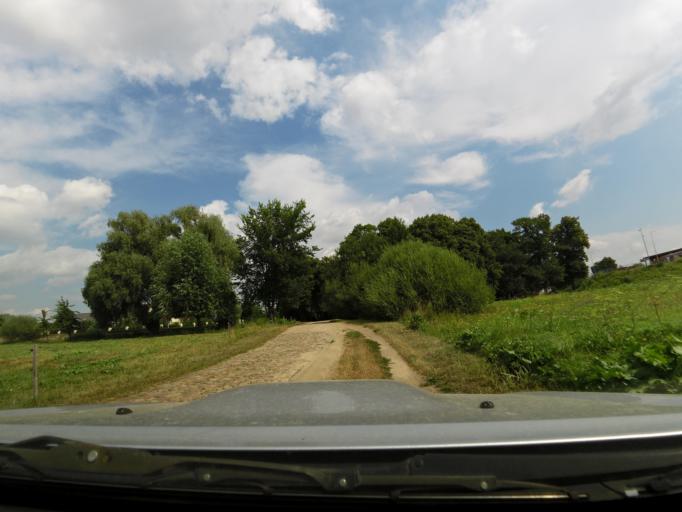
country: RU
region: Kaliningrad
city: Sovetsk
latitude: 55.0858
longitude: 21.9064
